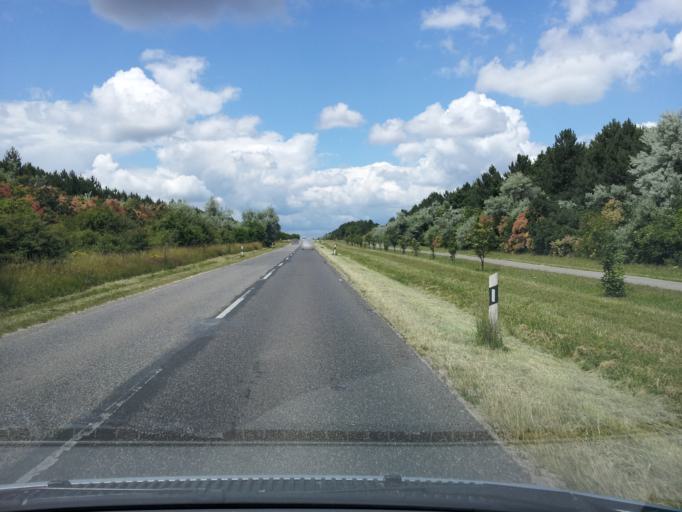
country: HU
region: Veszprem
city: Szentkiralyszabadja
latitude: 47.0631
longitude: 17.9581
